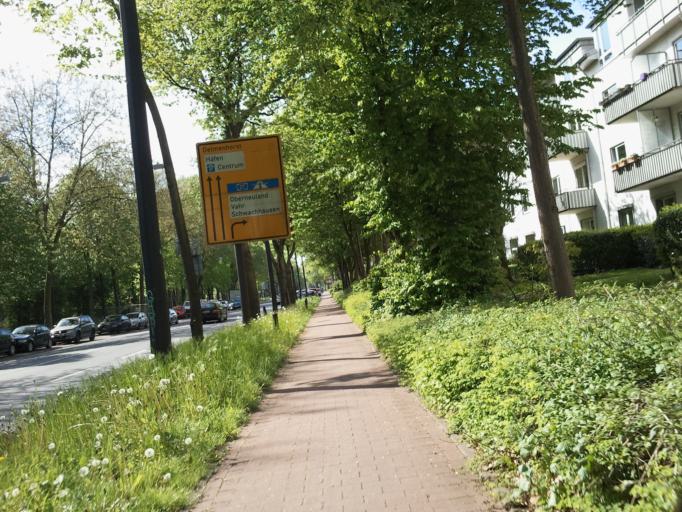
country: DE
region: Bremen
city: Bremen
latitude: 53.0730
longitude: 8.8557
